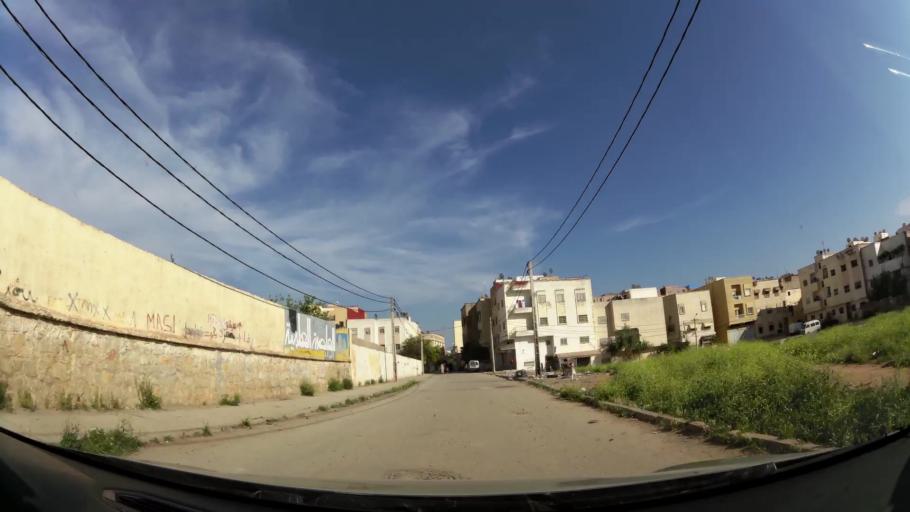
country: MA
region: Fes-Boulemane
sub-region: Fes
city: Fes
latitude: 34.0204
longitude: -5.0327
